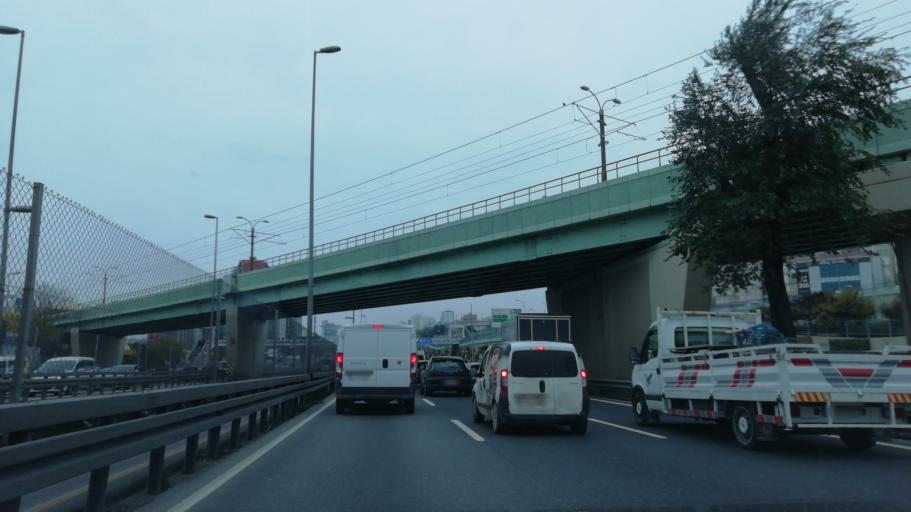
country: TR
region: Istanbul
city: guengoeren merter
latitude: 41.0063
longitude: 28.8955
